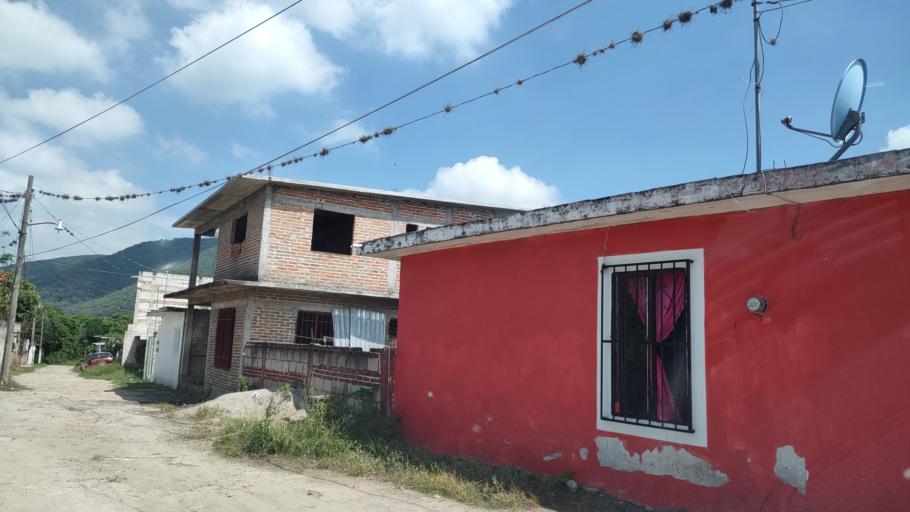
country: MX
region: Veracruz
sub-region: Emiliano Zapata
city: Dos Rios
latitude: 19.4295
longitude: -96.8082
